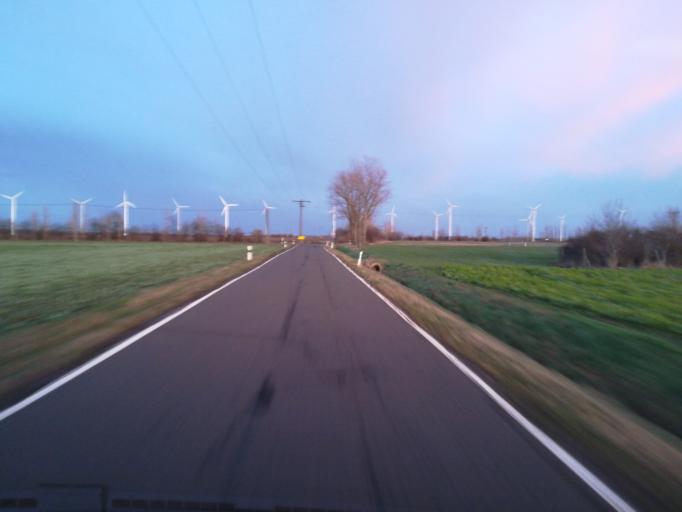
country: DE
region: Saxony-Anhalt
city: Roitzsch
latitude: 51.5563
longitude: 12.2712
